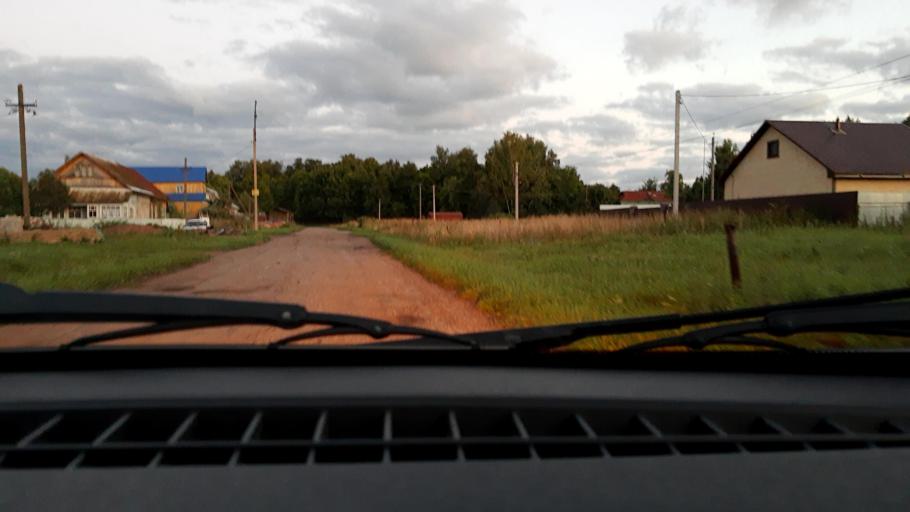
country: RU
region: Bashkortostan
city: Mikhaylovka
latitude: 54.8517
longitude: 55.8200
